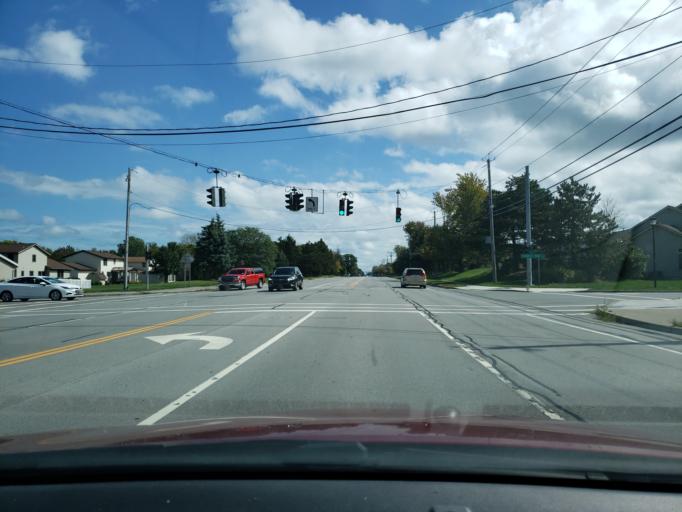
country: US
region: New York
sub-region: Monroe County
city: Greece
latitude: 43.2531
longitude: -77.7071
